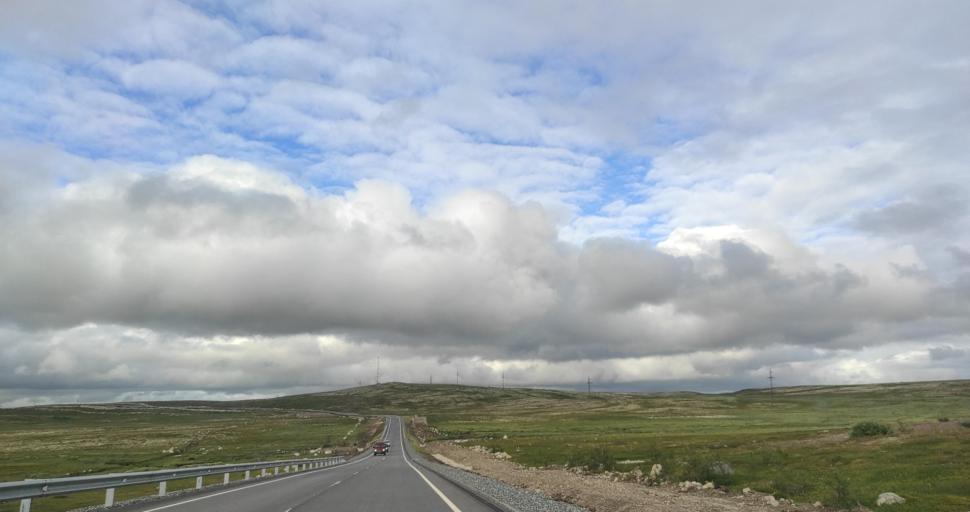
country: RU
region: Murmansk
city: Teriberka
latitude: 68.8653
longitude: 34.8819
